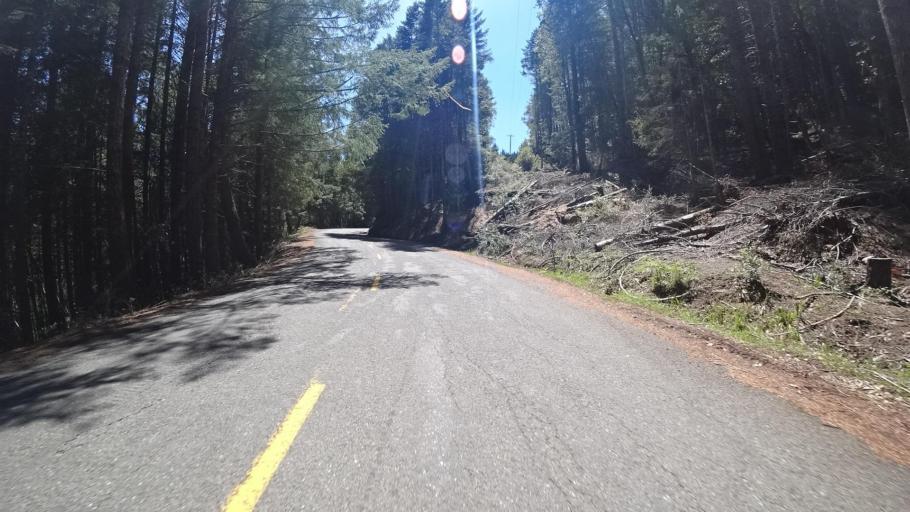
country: US
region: California
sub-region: Humboldt County
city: Rio Dell
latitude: 40.3112
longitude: -124.0612
